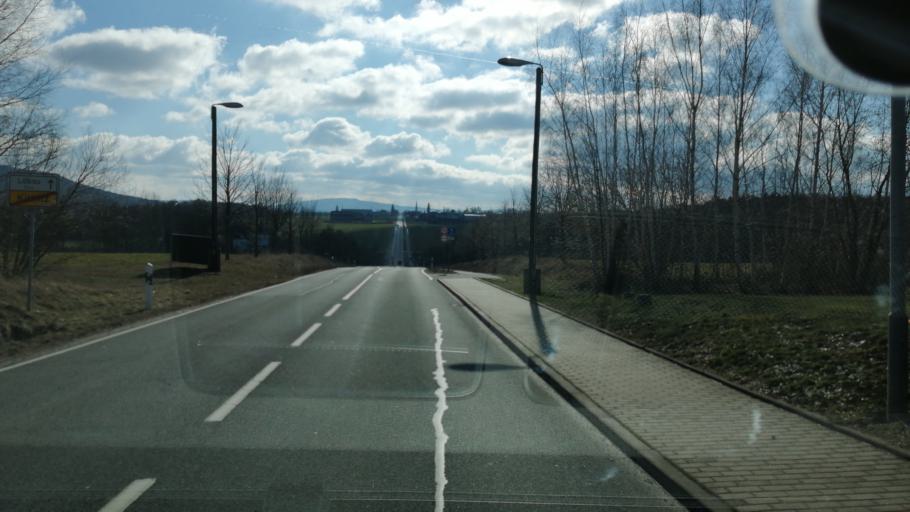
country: DE
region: Saxony
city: Lobau
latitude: 51.1205
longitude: 14.6744
